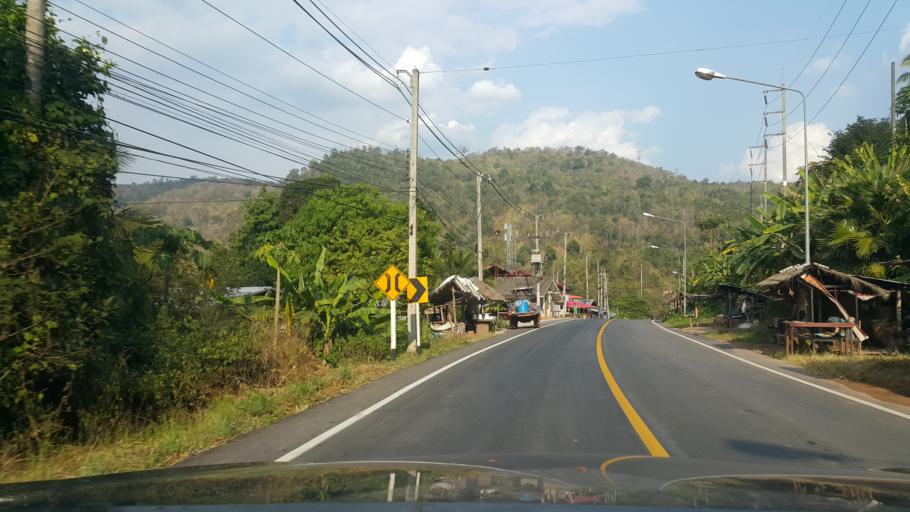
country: TH
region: Loei
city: Dan Sai
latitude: 17.2316
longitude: 101.0519
